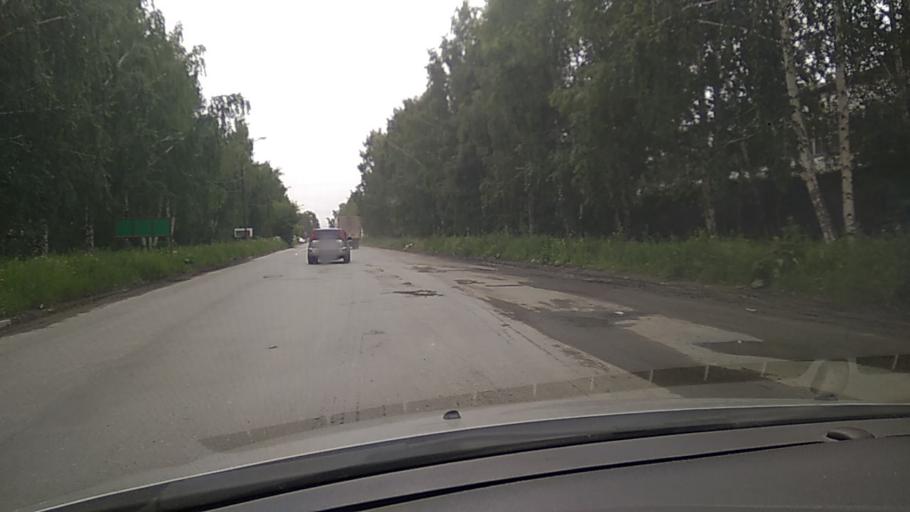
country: RU
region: Sverdlovsk
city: Shuvakish
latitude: 56.8916
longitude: 60.5174
